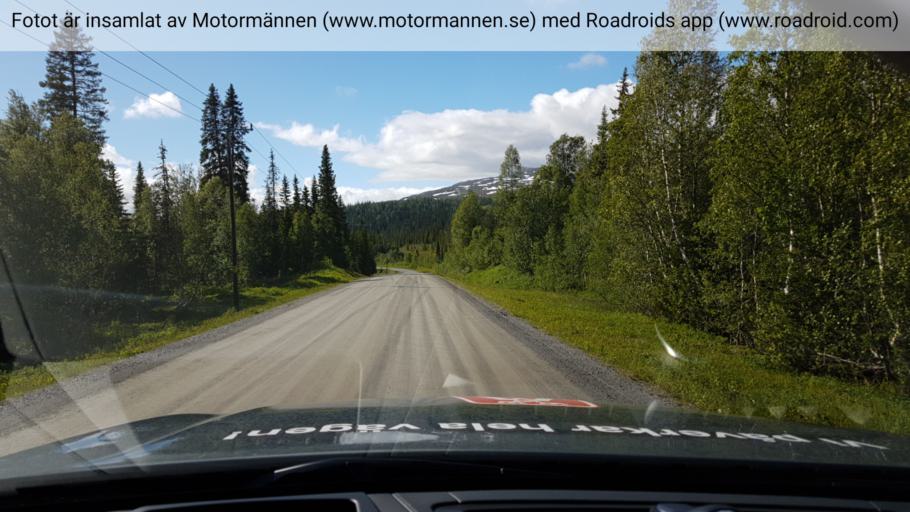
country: SE
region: Jaemtland
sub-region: Are Kommun
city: Are
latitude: 63.7020
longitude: 12.7678
